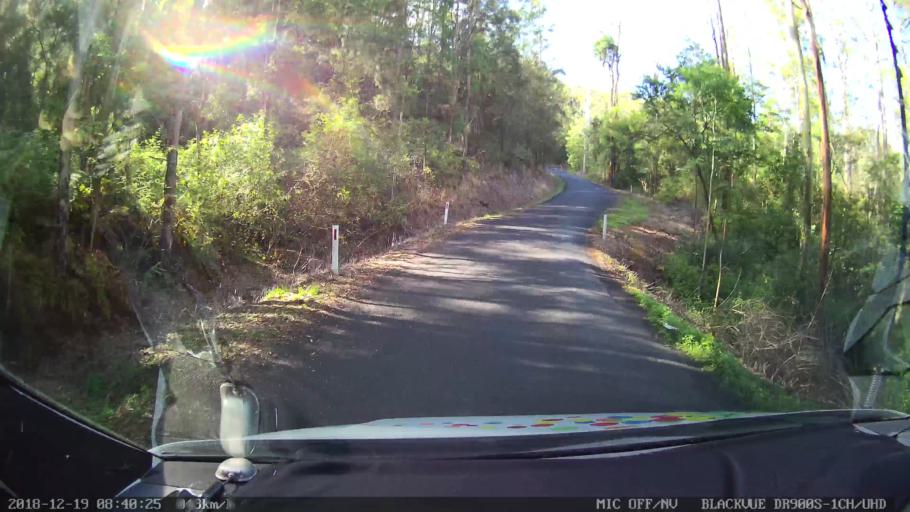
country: AU
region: New South Wales
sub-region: Kyogle
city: Kyogle
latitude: -28.3393
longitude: 152.9695
